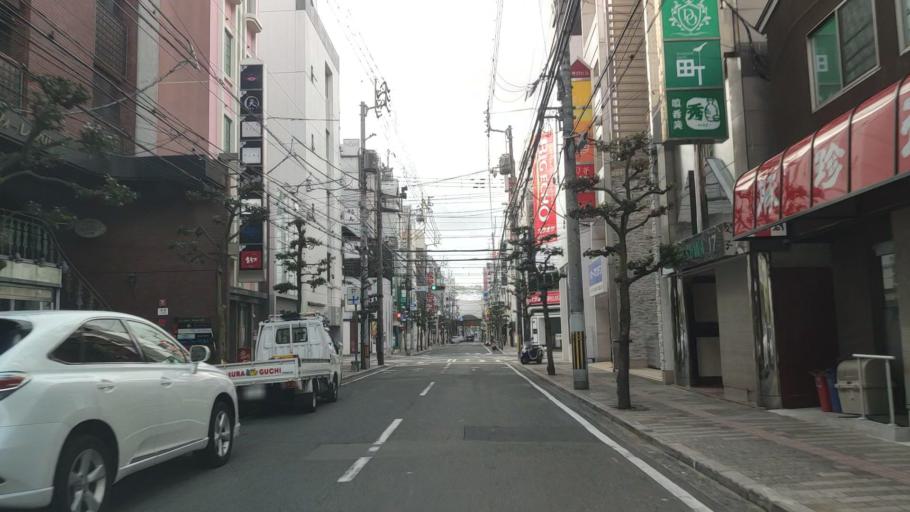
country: JP
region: Ehime
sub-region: Shikoku-chuo Shi
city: Matsuyama
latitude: 33.8400
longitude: 132.7727
